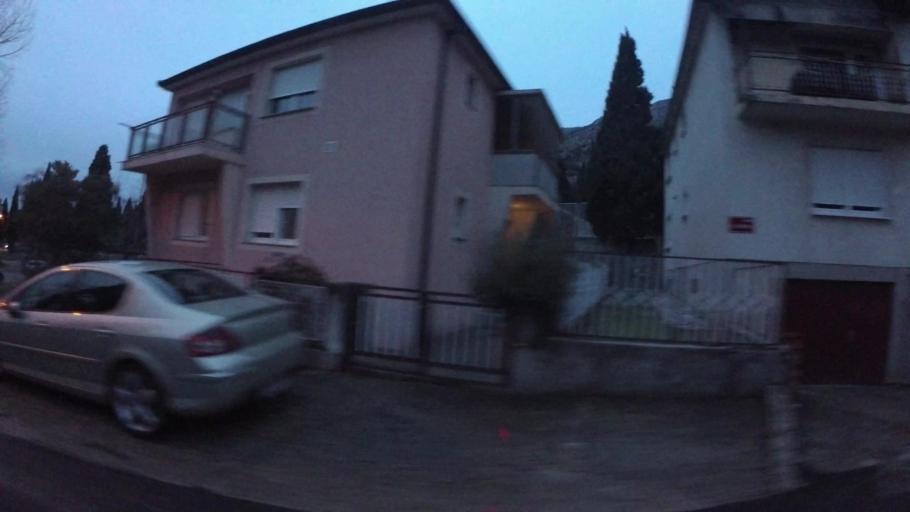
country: BA
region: Federation of Bosnia and Herzegovina
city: Rodoc
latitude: 43.3229
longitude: 17.8188
